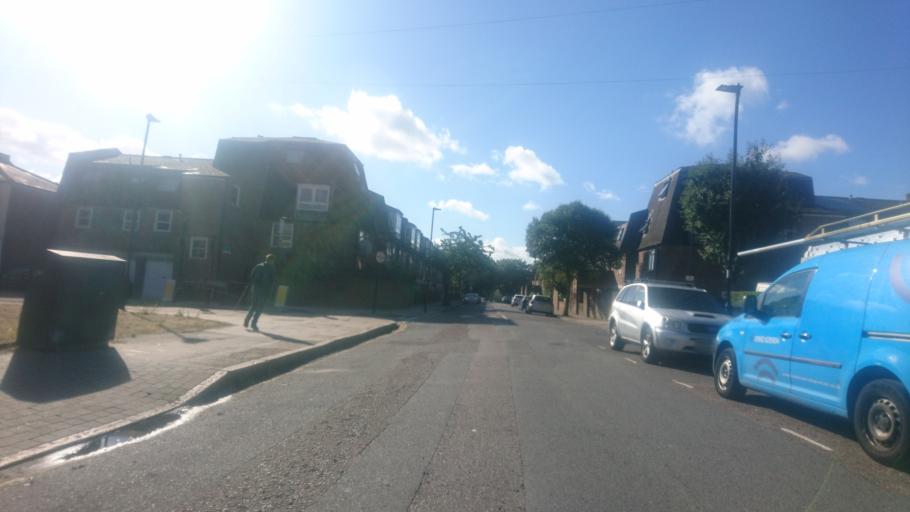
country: GB
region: England
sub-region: Greater London
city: Holloway
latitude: 51.5647
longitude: -0.1217
